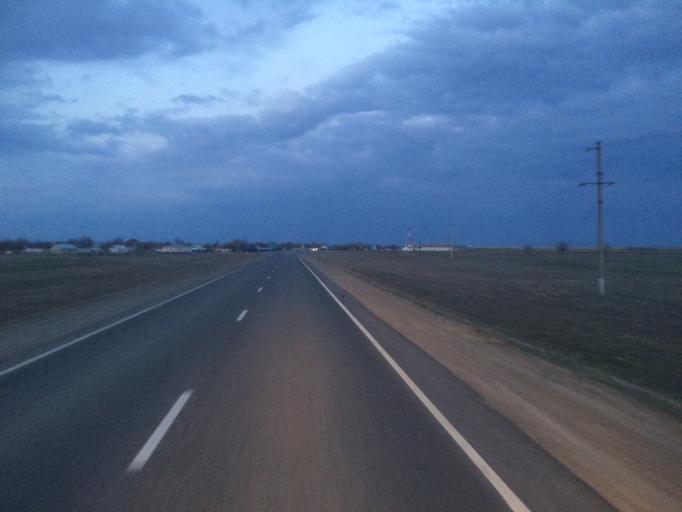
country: KZ
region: Aqtoebe
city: Martuk
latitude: 50.6402
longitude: 56.6842
